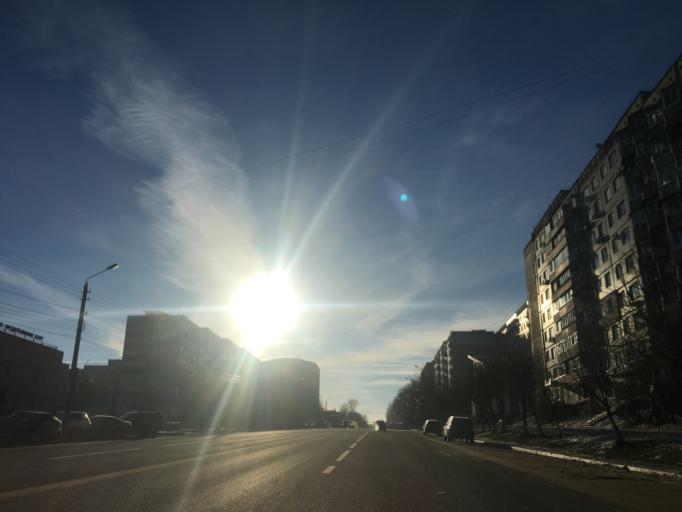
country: RU
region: Tula
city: Tula
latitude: 54.1952
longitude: 37.5904
